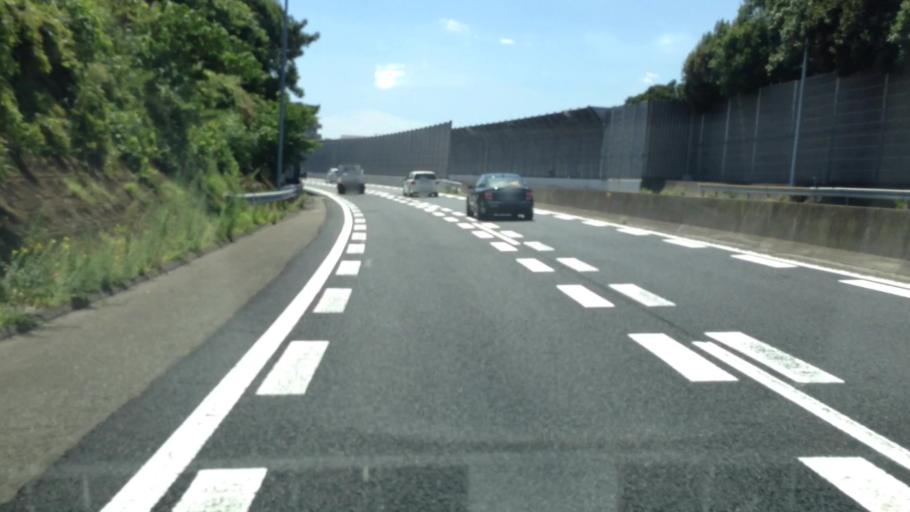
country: JP
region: Kanagawa
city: Yokohama
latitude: 35.4096
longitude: 139.5750
